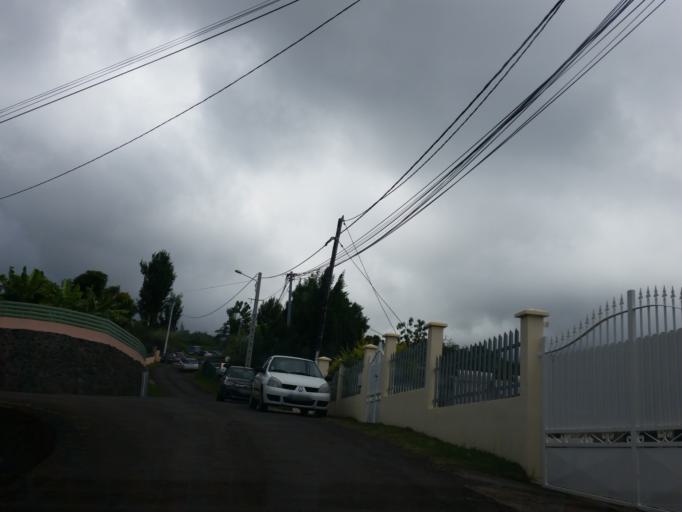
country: RE
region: Reunion
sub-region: Reunion
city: L'Entre-Deux
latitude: -21.2427
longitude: 55.4796
